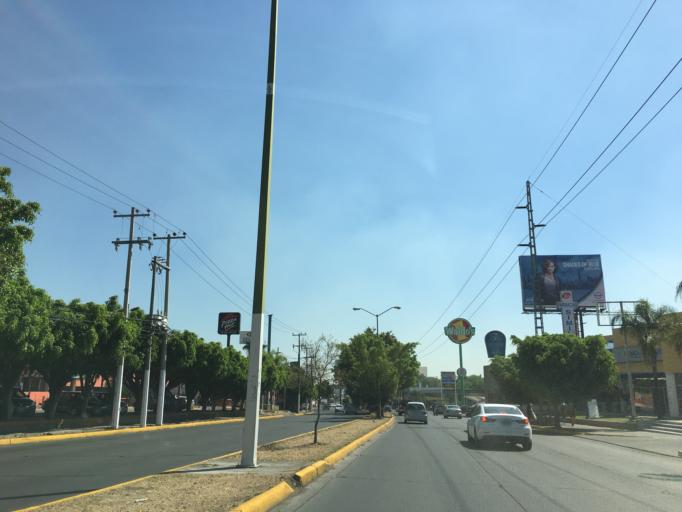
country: MX
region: Jalisco
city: Guadalajara
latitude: 20.6350
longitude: -103.3984
